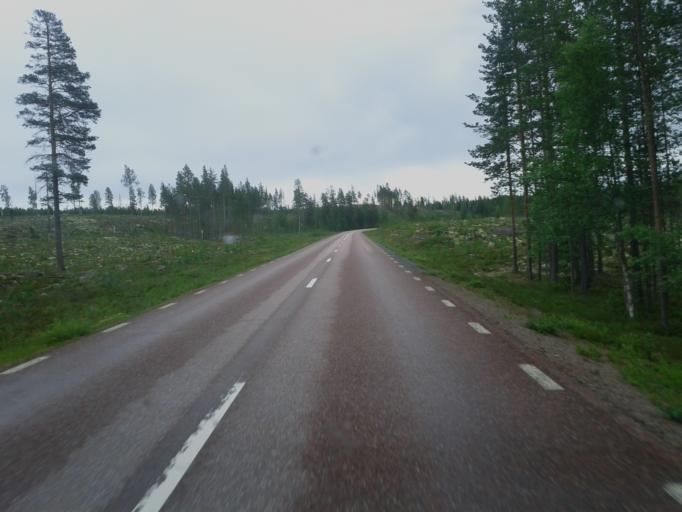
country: NO
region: Hedmark
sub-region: Trysil
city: Innbygda
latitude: 61.8208
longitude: 12.8924
